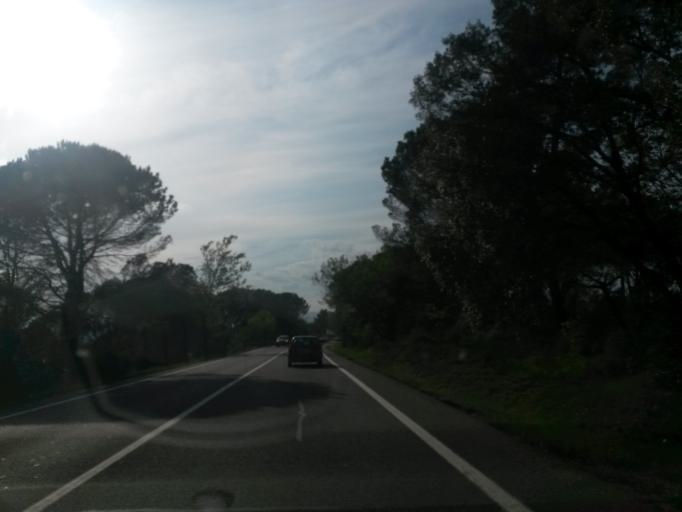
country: ES
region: Catalonia
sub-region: Provincia de Girona
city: Caldes de Malavella
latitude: 41.8477
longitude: 2.7766
